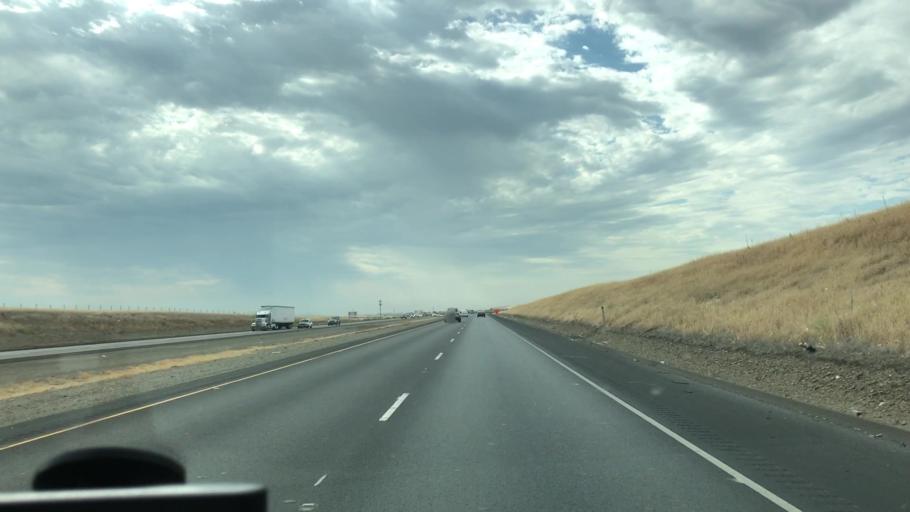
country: US
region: California
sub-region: San Joaquin County
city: Tracy
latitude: 37.6657
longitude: -121.4469
